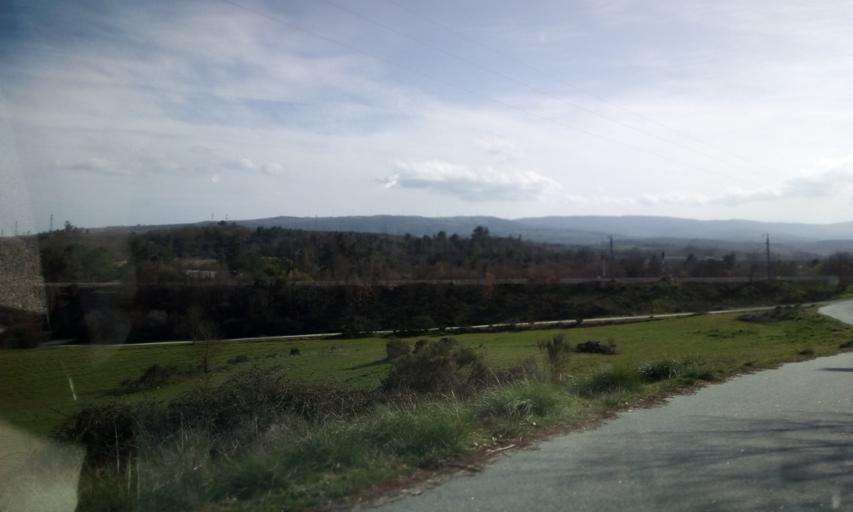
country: PT
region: Guarda
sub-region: Celorico da Beira
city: Celorico da Beira
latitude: 40.6445
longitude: -7.4285
